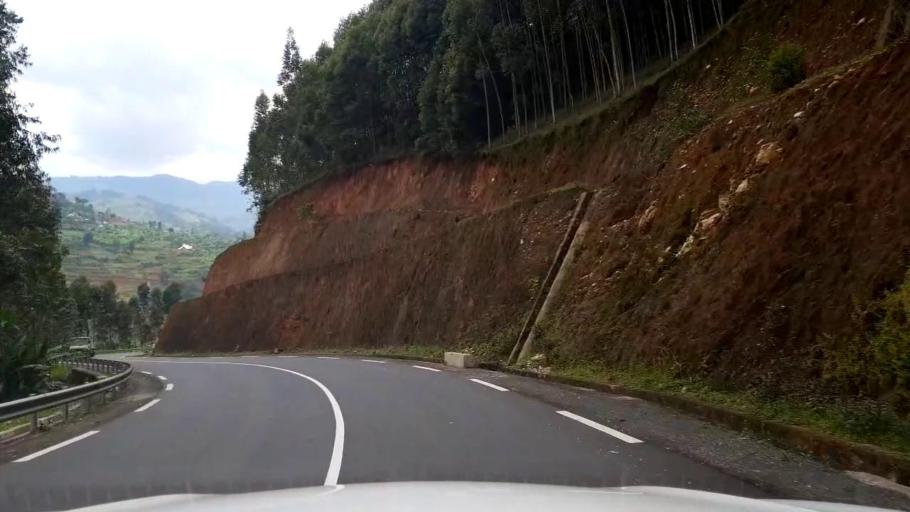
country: RW
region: Western Province
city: Kibuye
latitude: -1.9091
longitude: 29.3649
